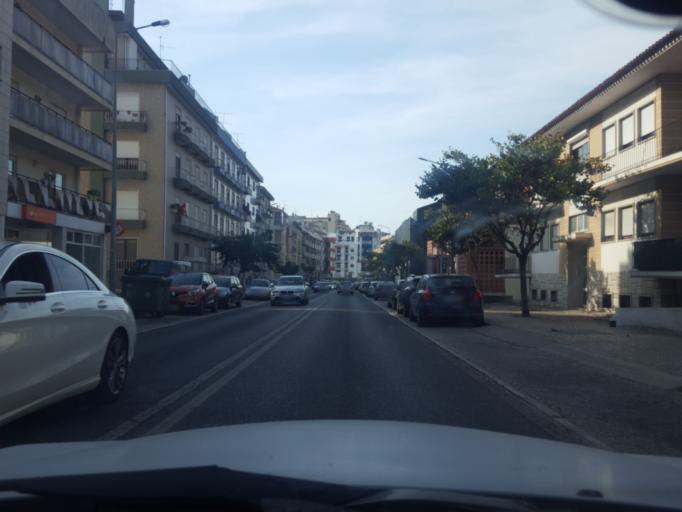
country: PT
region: Leiria
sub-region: Leiria
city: Leiria
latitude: 39.7378
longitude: -8.8007
